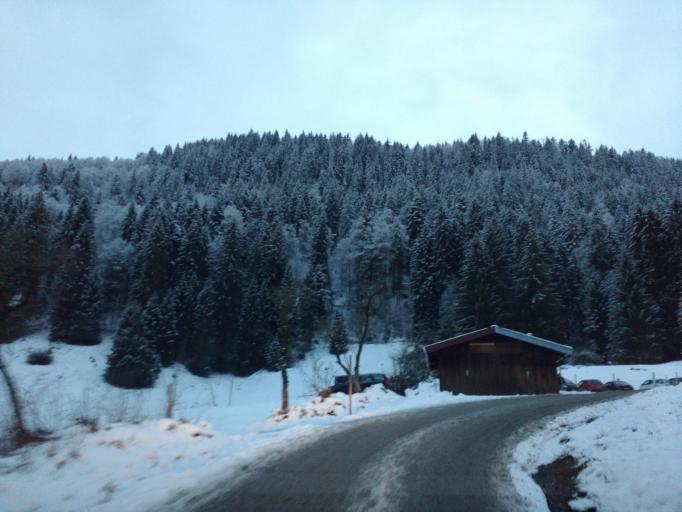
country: DE
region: Bavaria
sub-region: Swabia
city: Obermaiselstein
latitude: 47.3995
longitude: 10.2232
